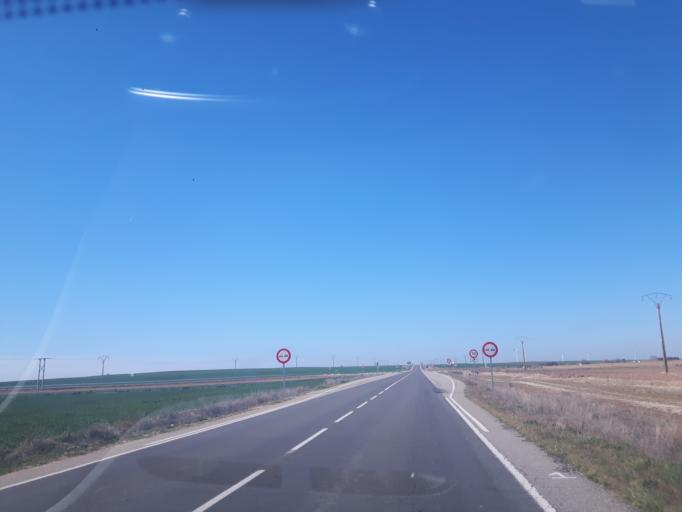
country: ES
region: Castille and Leon
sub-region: Provincia de Salamanca
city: Coca de Alba
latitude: 40.8721
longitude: -5.3751
